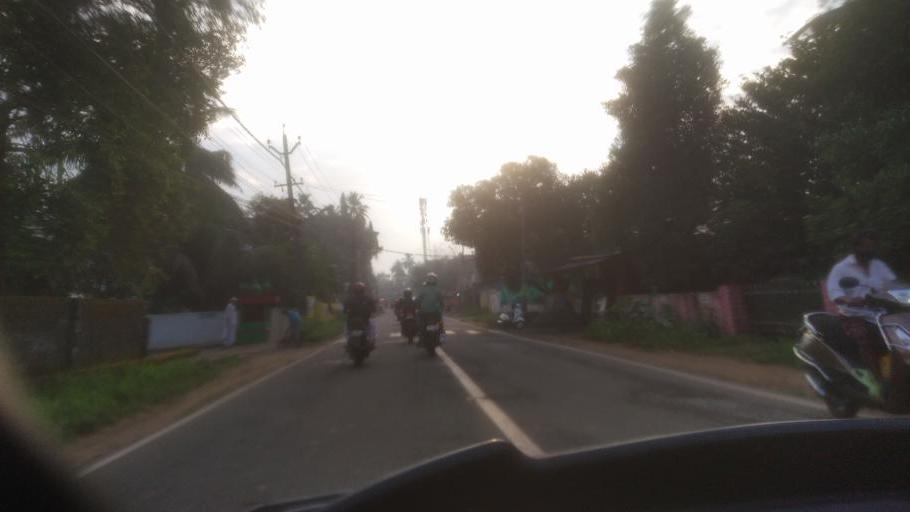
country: IN
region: Kerala
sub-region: Ernakulam
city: Perumpavur
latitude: 10.1168
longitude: 76.4449
